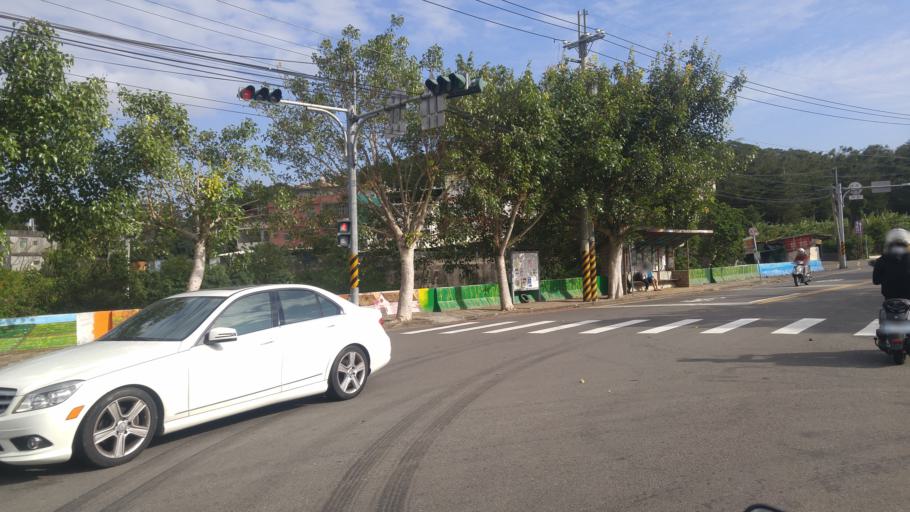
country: TW
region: Taiwan
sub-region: Hsinchu
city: Hsinchu
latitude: 24.7749
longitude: 120.9441
